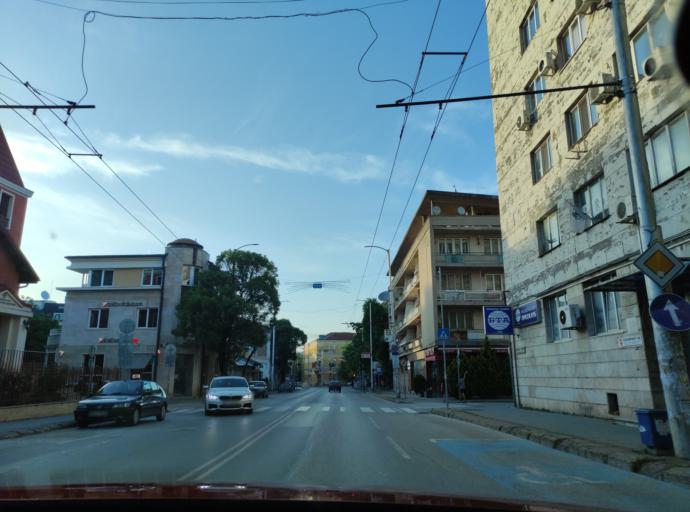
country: BG
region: Pleven
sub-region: Obshtina Pleven
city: Pleven
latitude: 43.4094
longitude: 24.6200
